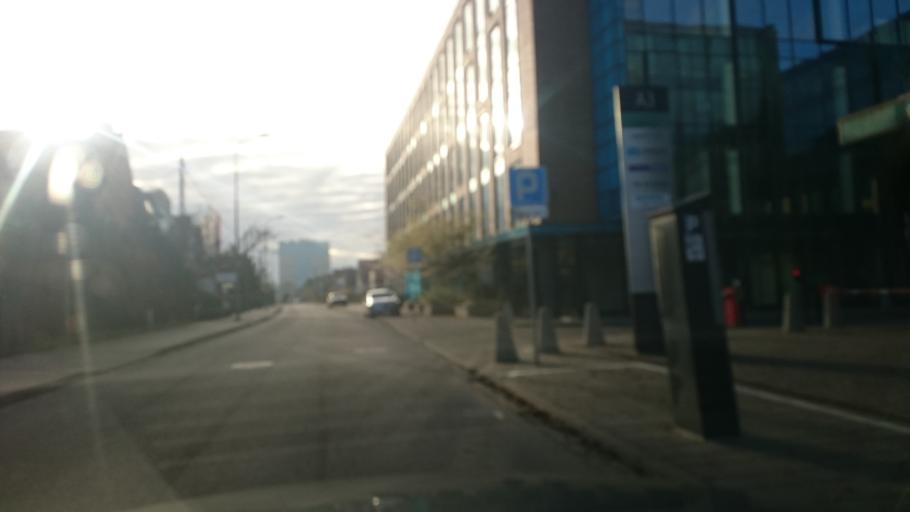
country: PL
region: Pomeranian Voivodeship
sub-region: Sopot
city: Sopot
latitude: 54.4056
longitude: 18.5775
